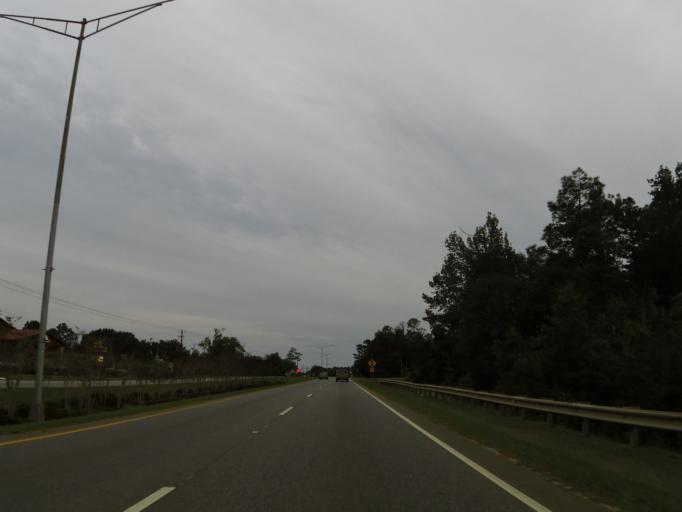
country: US
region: Alabama
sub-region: Baldwin County
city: Bay Minette
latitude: 30.8567
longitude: -87.7767
